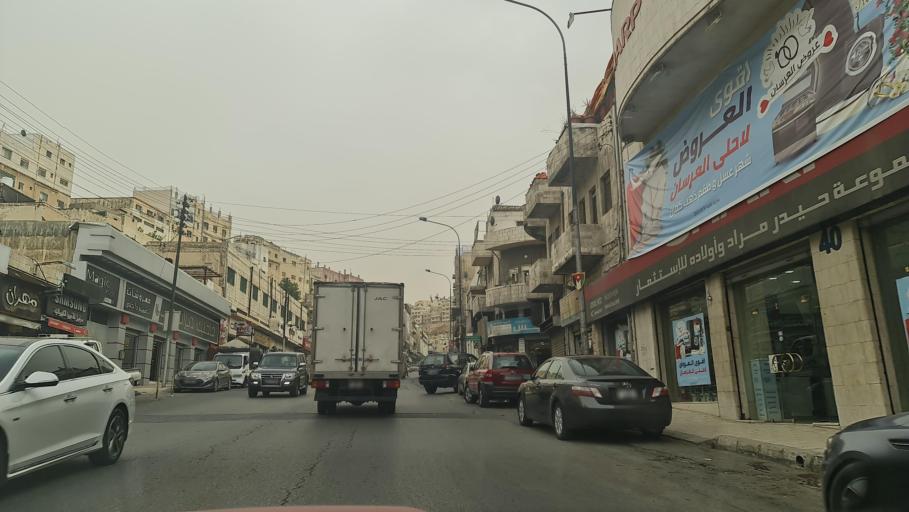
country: JO
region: Amman
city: Amman
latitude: 31.9420
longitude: 35.9292
